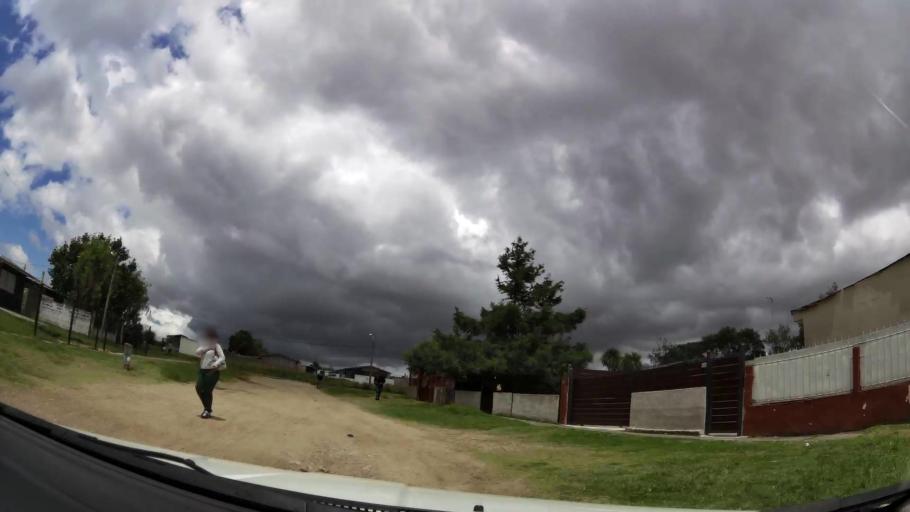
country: UY
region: Montevideo
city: Montevideo
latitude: -34.8300
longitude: -56.1667
